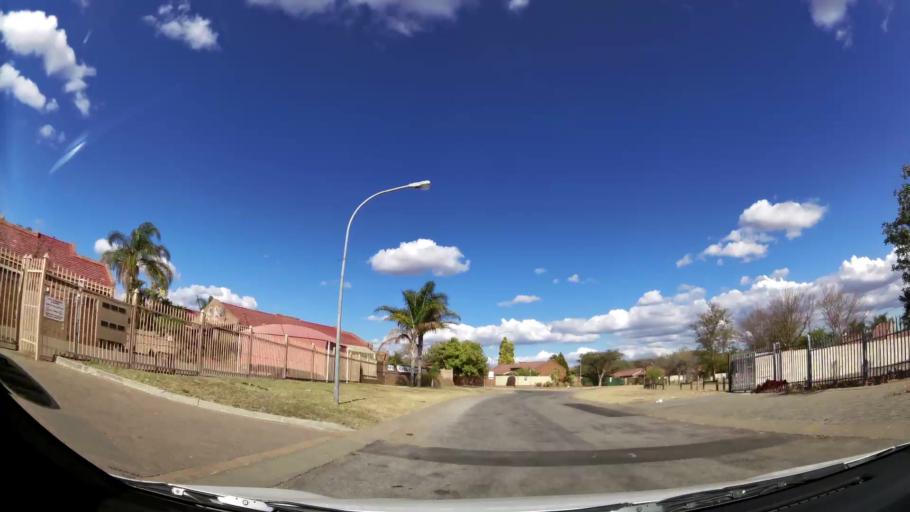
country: ZA
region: Limpopo
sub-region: Capricorn District Municipality
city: Polokwane
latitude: -23.8869
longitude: 29.4713
